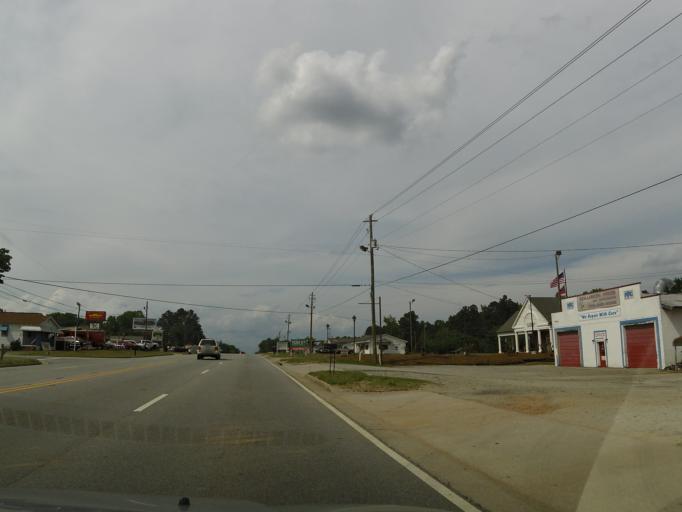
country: US
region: Georgia
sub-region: McDuffie County
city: Thomson
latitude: 33.4936
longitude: -82.5042
